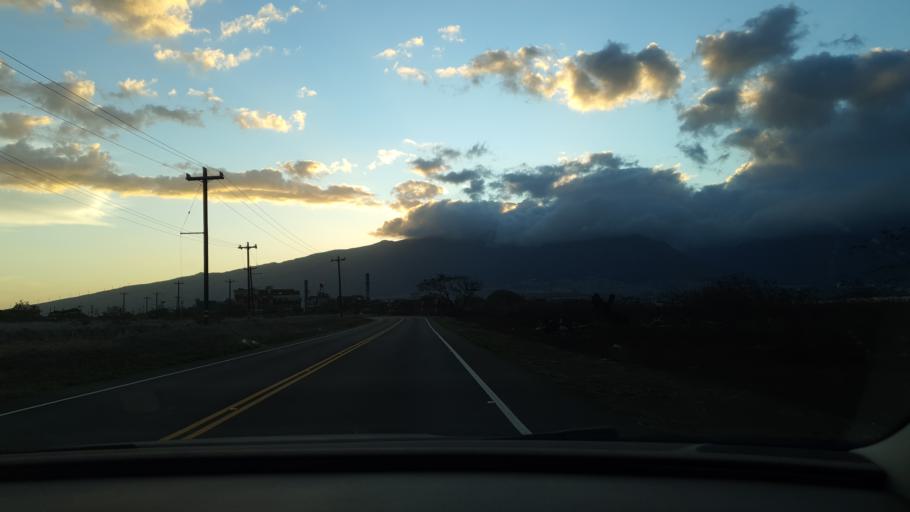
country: US
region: Hawaii
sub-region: Maui County
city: Kahului
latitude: 20.8710
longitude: -156.4463
